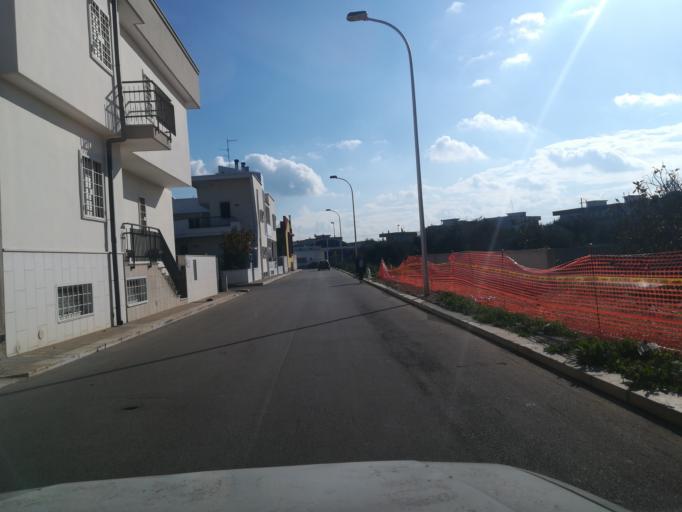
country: IT
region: Apulia
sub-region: Provincia di Bari
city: Modugno
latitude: 41.0770
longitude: 16.7788
